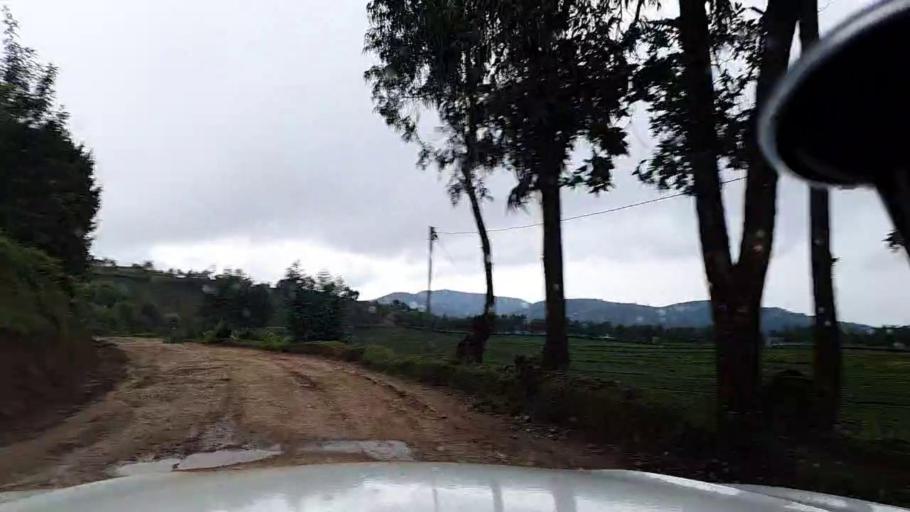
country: RW
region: Western Province
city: Kibuye
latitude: -2.0924
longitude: 29.4945
